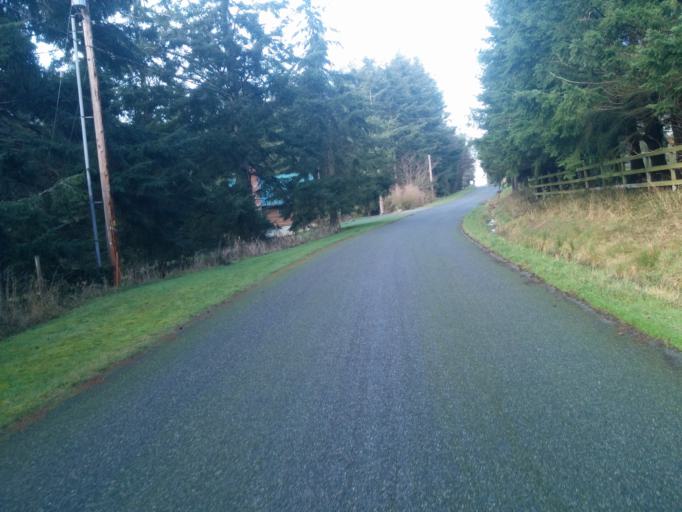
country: US
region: Washington
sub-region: Island County
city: Freeland
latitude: 48.0439
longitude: -122.4978
